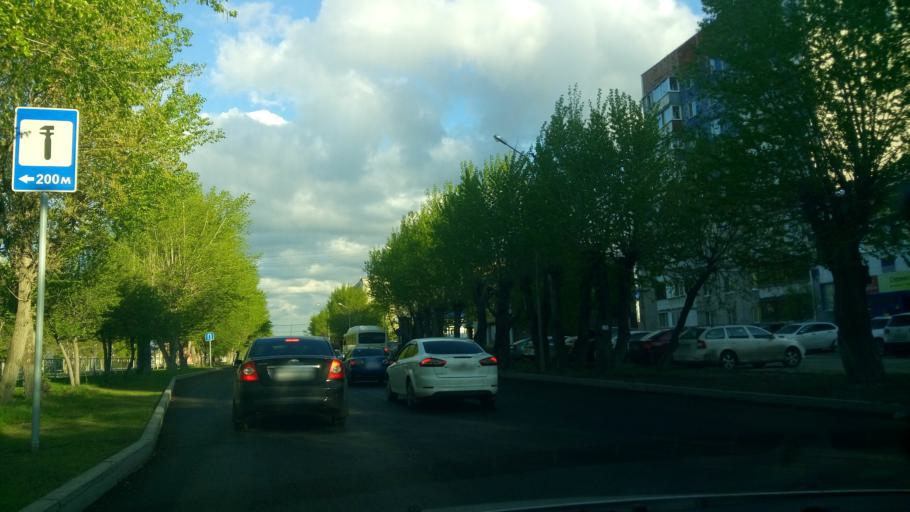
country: RU
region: Tjumen
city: Tyumen
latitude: 57.1358
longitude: 65.6000
